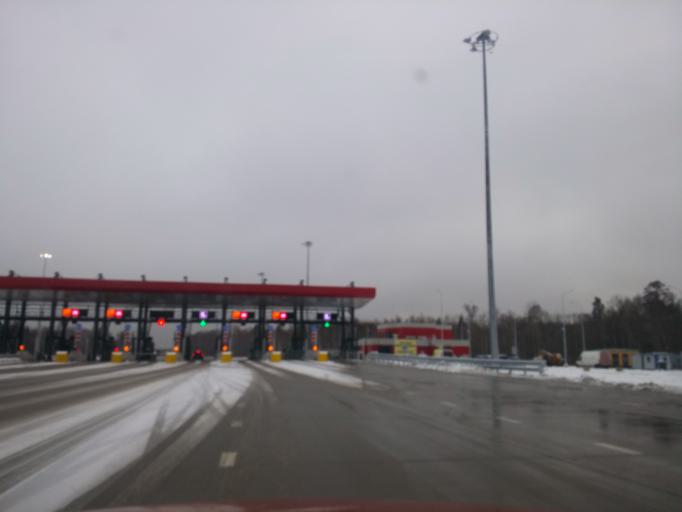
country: RU
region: Tverskaya
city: Likhoslavl'
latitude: 56.9558
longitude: 35.5053
